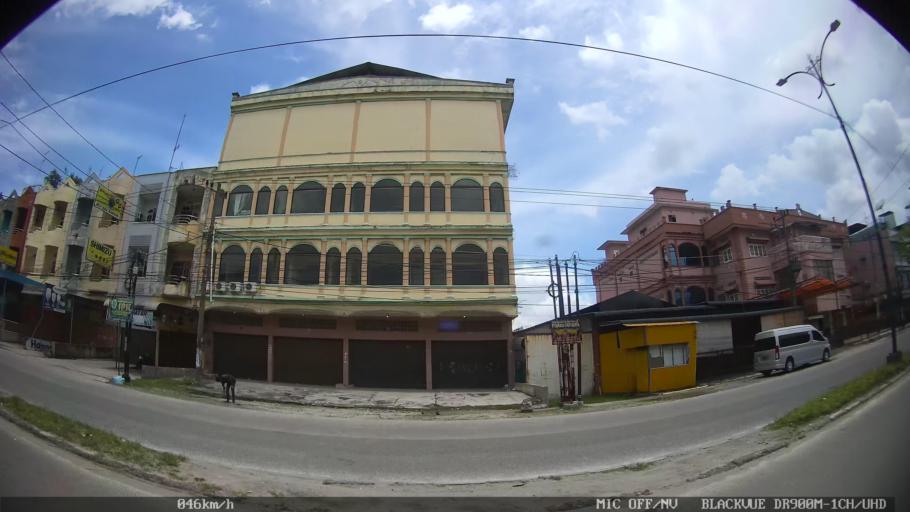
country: ID
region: North Sumatra
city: Medan
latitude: 3.6203
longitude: 98.6808
